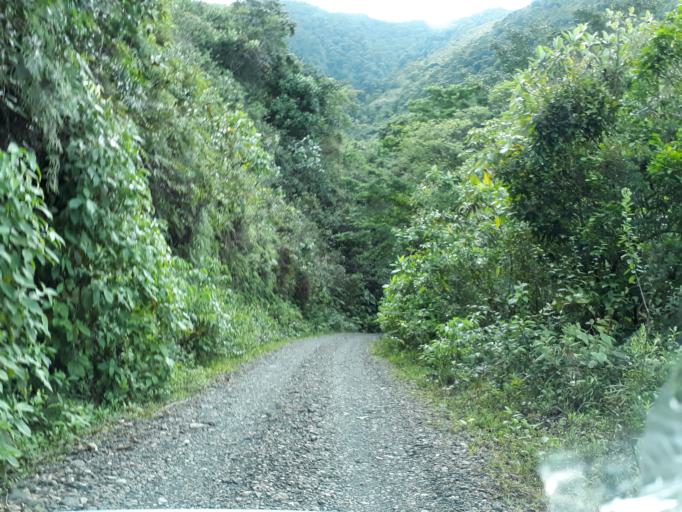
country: CO
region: Boyaca
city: Chivor
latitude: 4.7279
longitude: -73.3577
